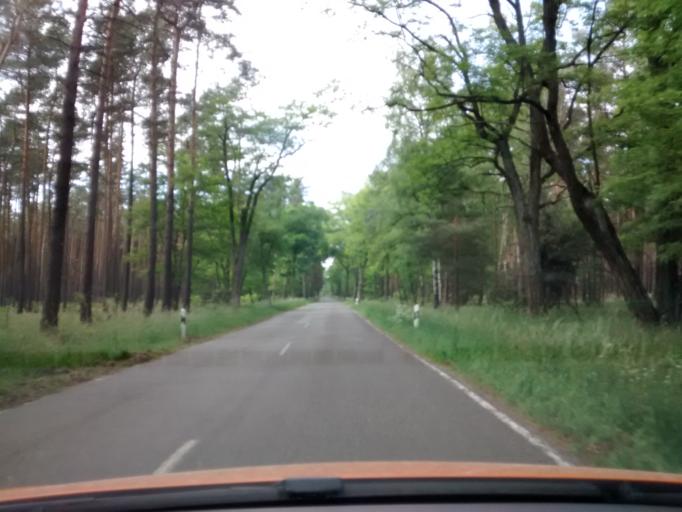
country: DE
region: Brandenburg
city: Ihlow
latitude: 51.9668
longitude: 13.3174
